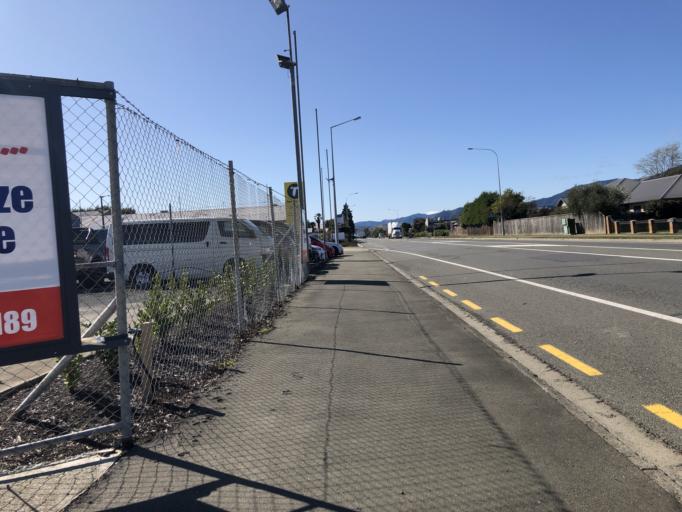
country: NZ
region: Tasman
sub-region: Tasman District
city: Richmond
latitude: -41.3428
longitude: 173.1717
